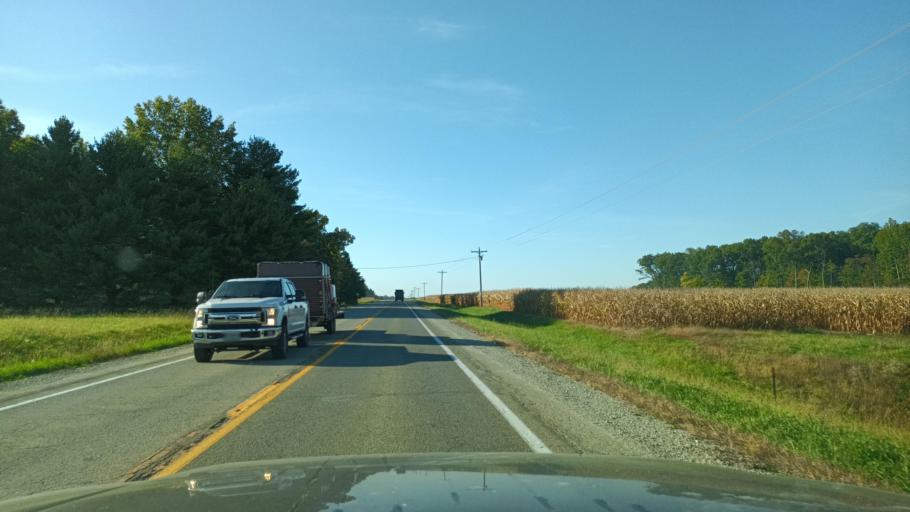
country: US
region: Illinois
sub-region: Clark County
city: Marshall
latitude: 39.4663
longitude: -87.6820
